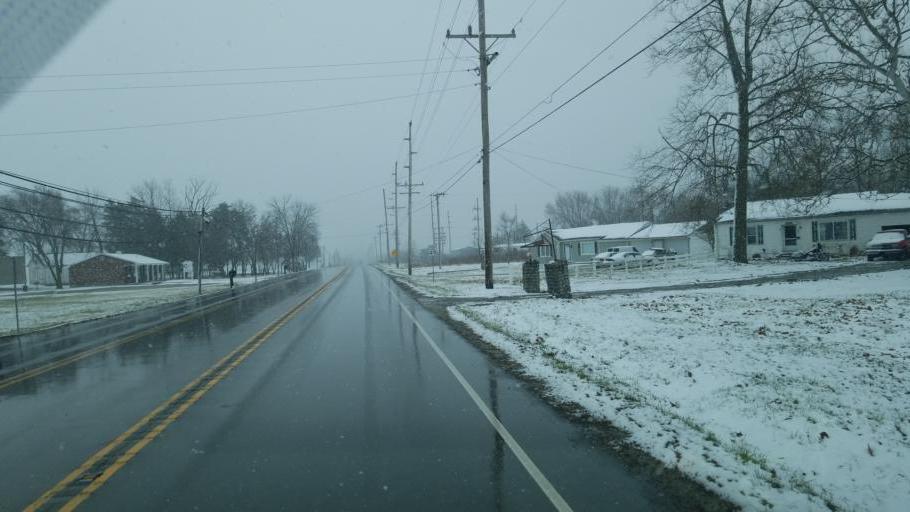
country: US
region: Indiana
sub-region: Wayne County
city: Richmond
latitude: 39.8781
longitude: -84.9409
